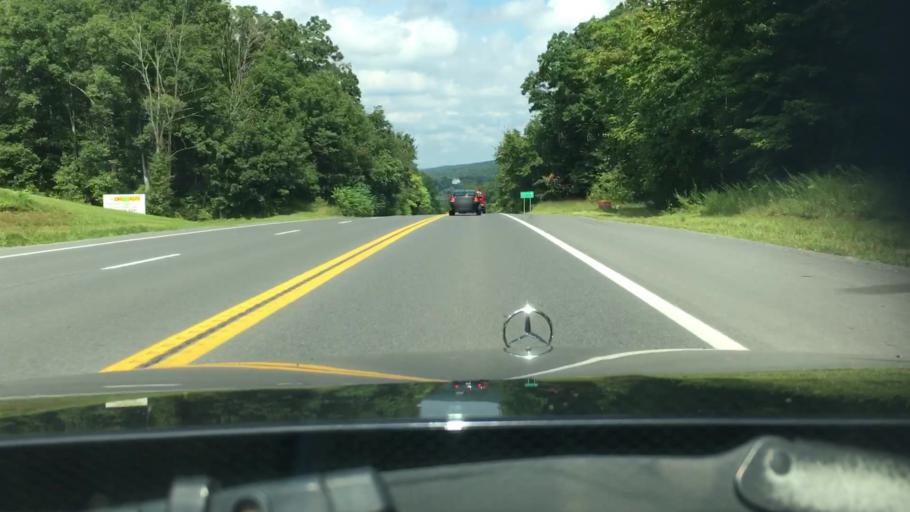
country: US
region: Maryland
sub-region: Washington County
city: Hancock
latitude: 39.6863
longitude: -78.1882
